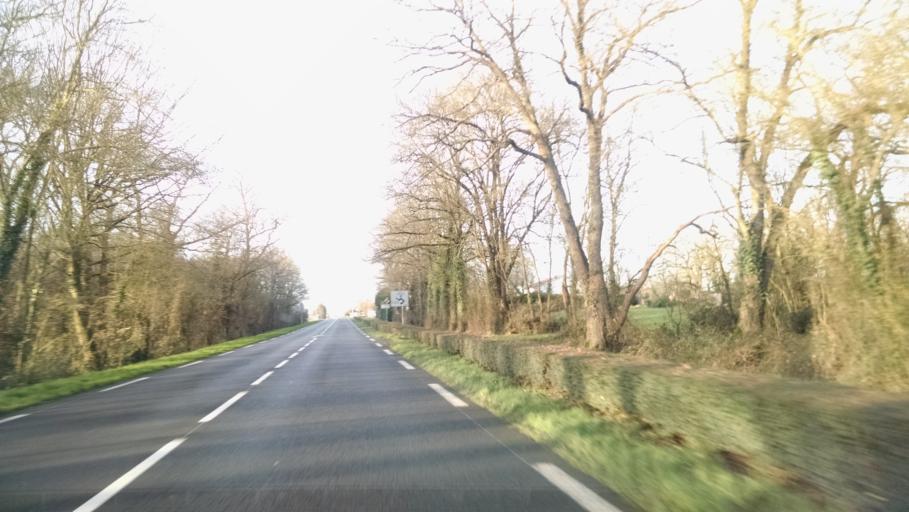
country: FR
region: Pays de la Loire
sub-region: Departement de la Vendee
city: Saint-Hilaire-de-Loulay
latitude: 46.9934
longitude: -1.3257
